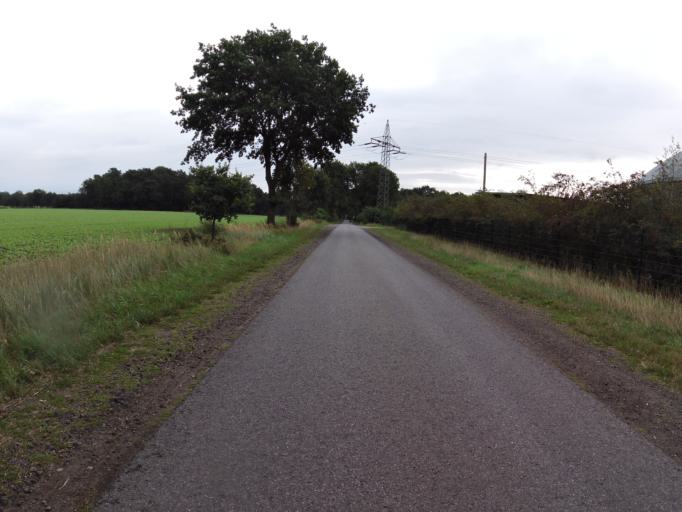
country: DE
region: Lower Saxony
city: Scheessel
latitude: 53.1886
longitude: 9.4768
